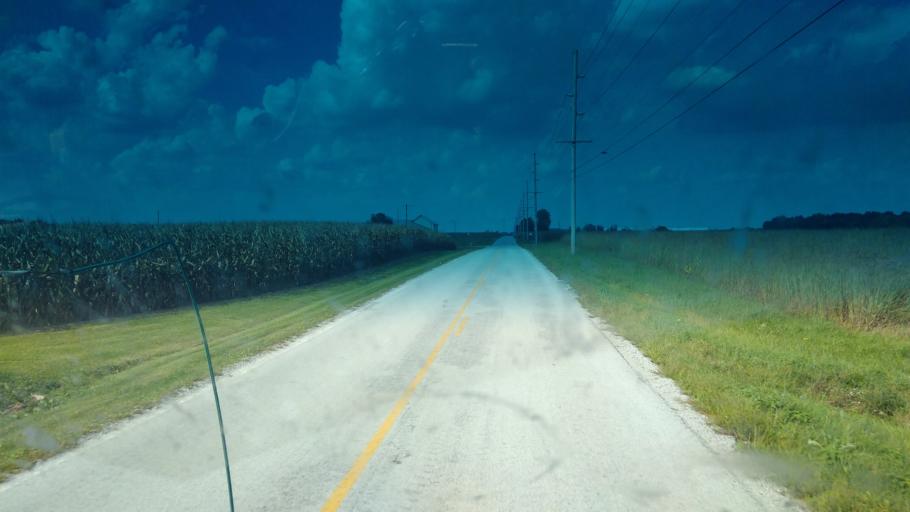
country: US
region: Ohio
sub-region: Hardin County
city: Kenton
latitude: 40.7598
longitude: -83.6523
